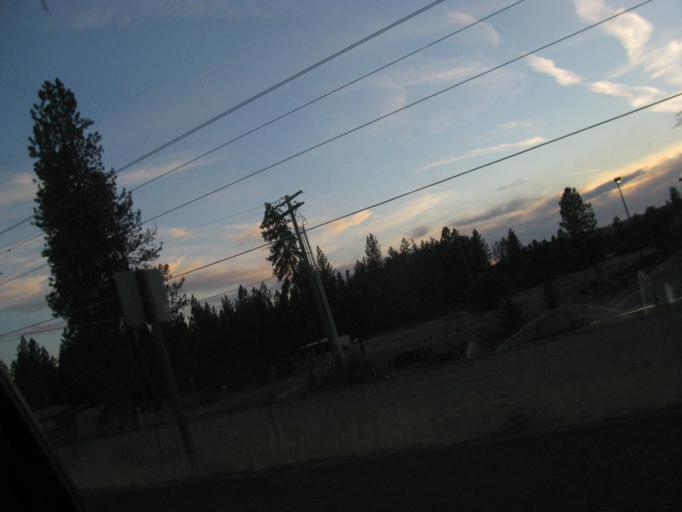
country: US
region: Washington
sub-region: Spokane County
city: Mead
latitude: 47.8097
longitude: -117.3473
